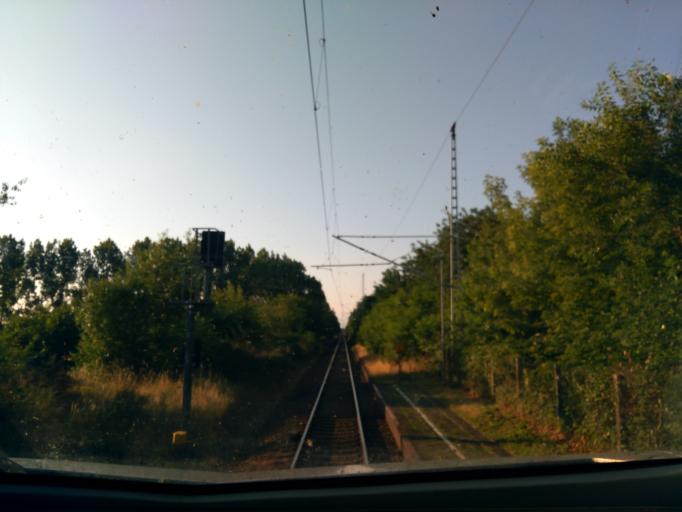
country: DE
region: Brandenburg
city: Vetschau
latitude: 51.8151
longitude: 14.0334
